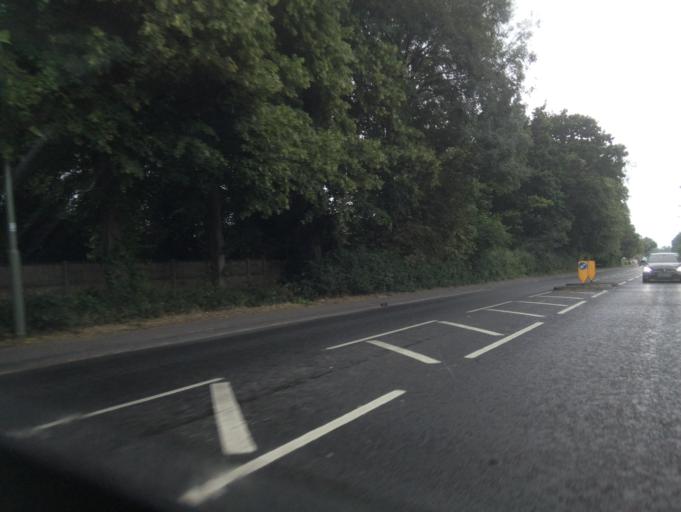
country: GB
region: England
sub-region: Surrey
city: Horley
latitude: 51.1795
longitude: -0.1654
